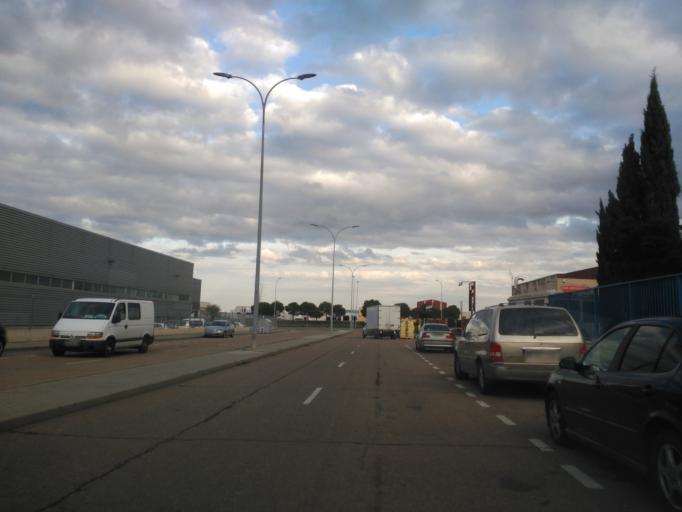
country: ES
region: Castille and Leon
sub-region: Provincia de Salamanca
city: Carbajosa de la Sagrada
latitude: 40.9371
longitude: -5.6652
